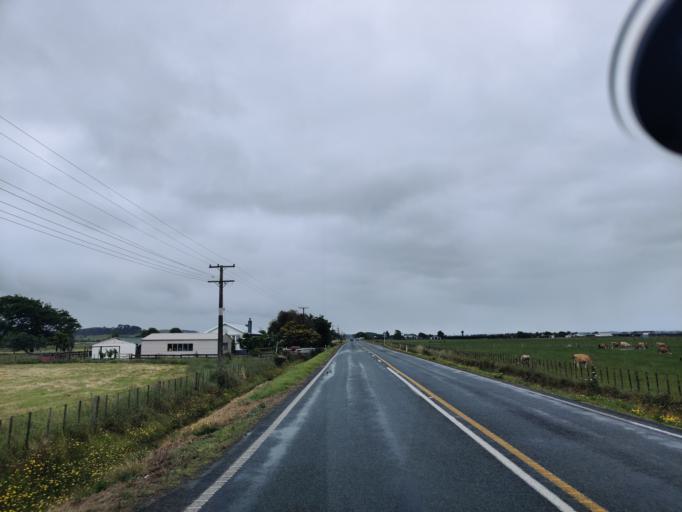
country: NZ
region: Northland
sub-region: Kaipara District
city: Dargaville
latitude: -35.9520
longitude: 173.8934
